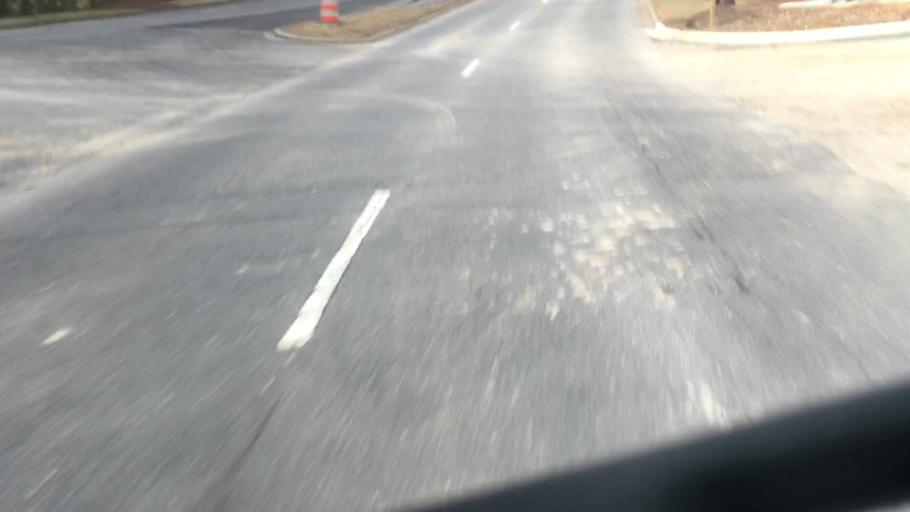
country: US
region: Alabama
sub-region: Jefferson County
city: Cahaba Heights
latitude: 33.4847
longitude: -86.7081
